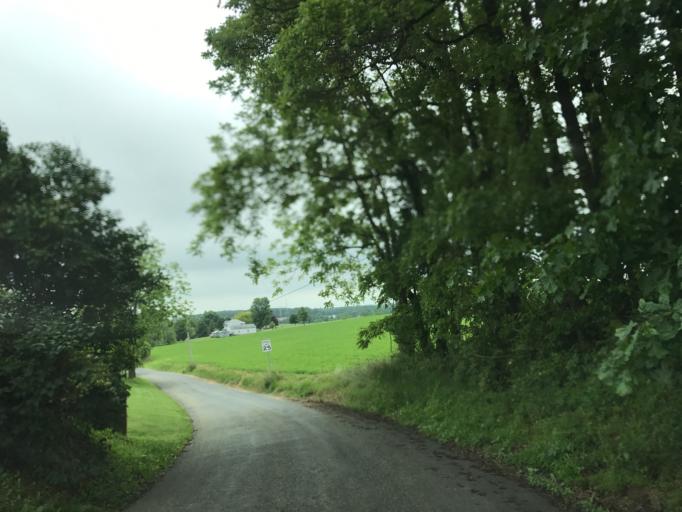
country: US
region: Maryland
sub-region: Harford County
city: Jarrettsville
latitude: 39.6973
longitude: -76.5088
